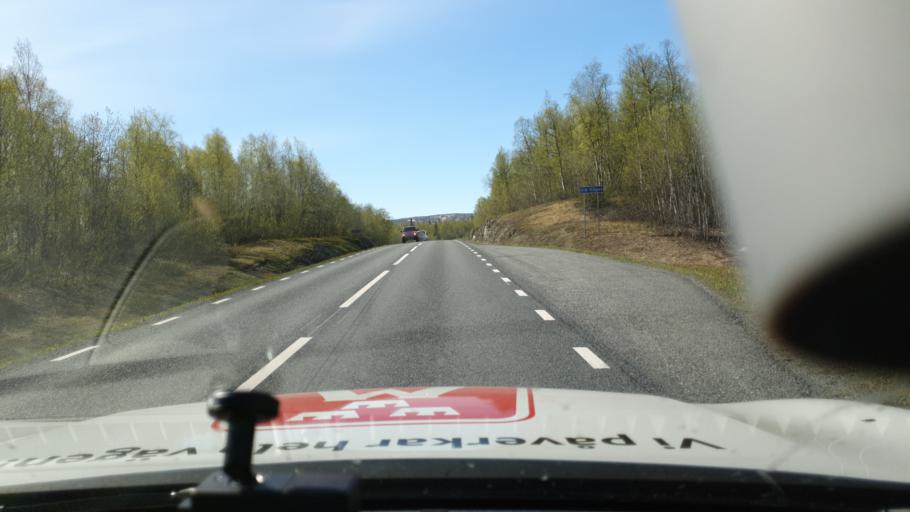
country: NO
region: Nordland
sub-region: Rana
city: Mo i Rana
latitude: 65.7646
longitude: 15.1147
